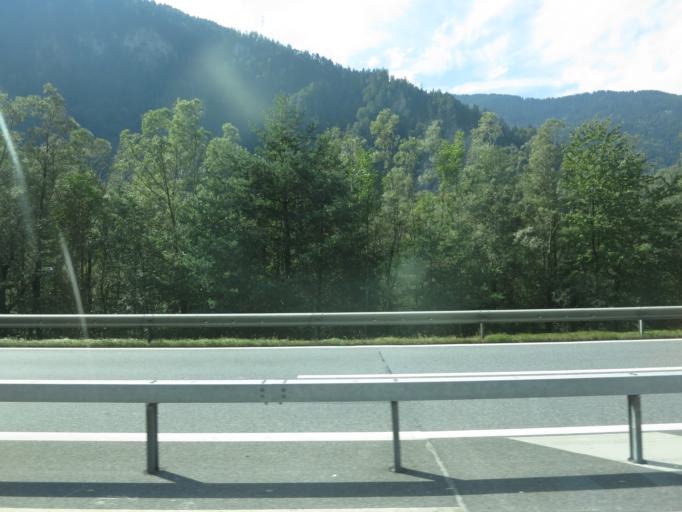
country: CH
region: Grisons
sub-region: Imboden District
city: Rhazuns
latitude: 46.7786
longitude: 9.4168
